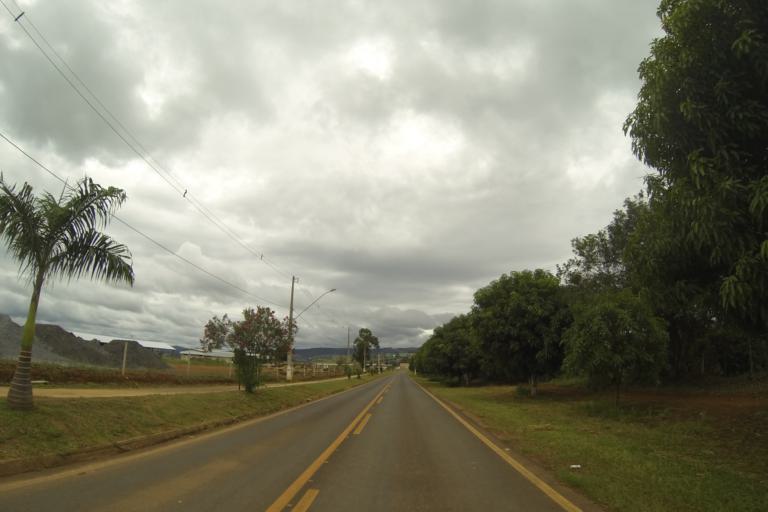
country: BR
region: Minas Gerais
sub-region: Bambui
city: Bambui
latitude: -20.0041
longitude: -46.2102
